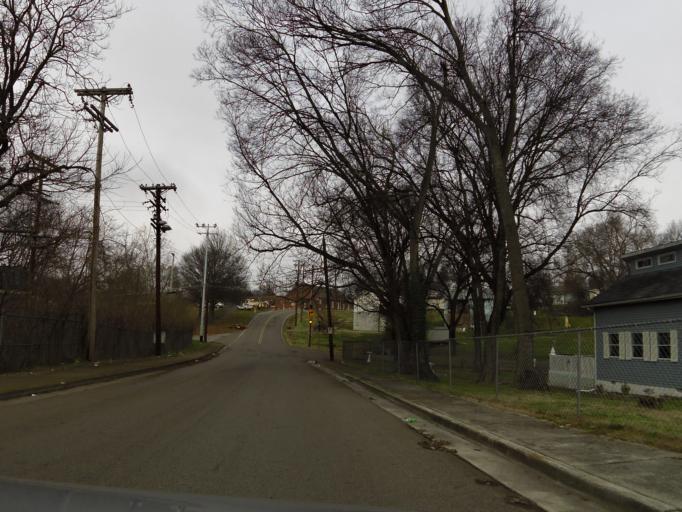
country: US
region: Tennessee
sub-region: Knox County
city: Knoxville
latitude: 35.9730
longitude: -83.9442
